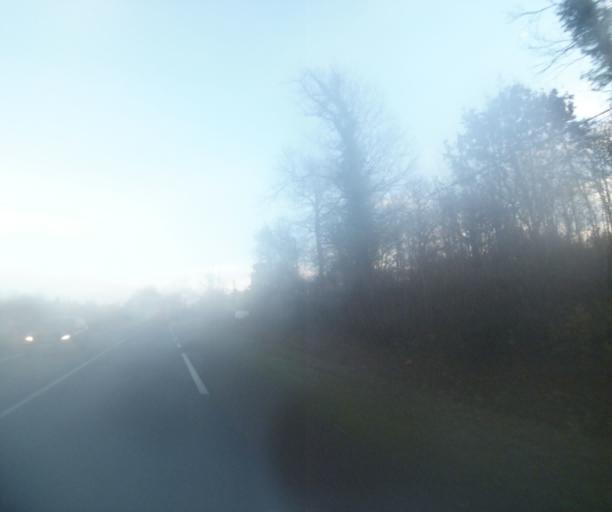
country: FR
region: Poitou-Charentes
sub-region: Departement de la Charente-Maritime
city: Fontcouverte
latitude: 45.7579
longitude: -0.5911
